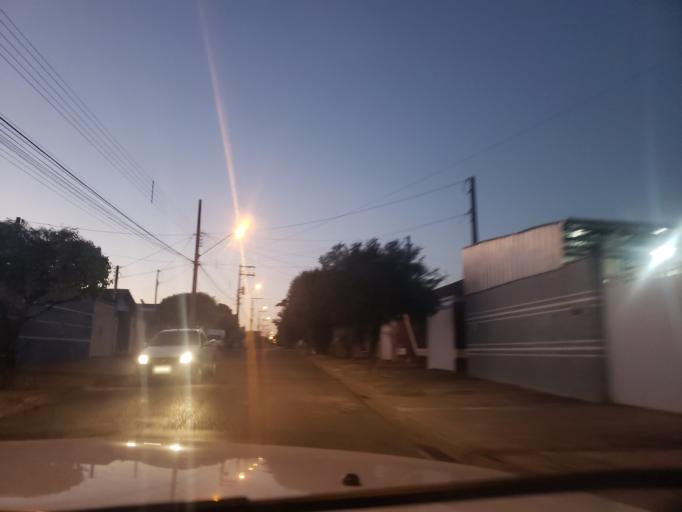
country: BR
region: Sao Paulo
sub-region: Conchal
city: Conchal
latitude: -22.2965
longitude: -47.1315
